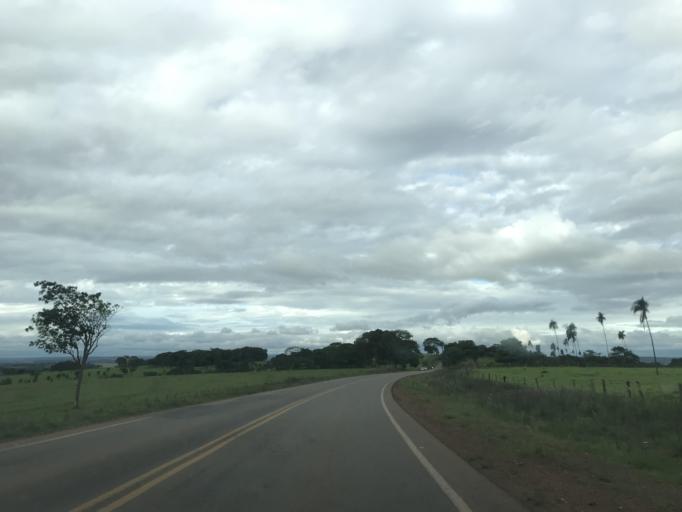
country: BR
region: Goias
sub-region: Vianopolis
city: Vianopolis
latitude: -16.7139
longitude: -48.4037
